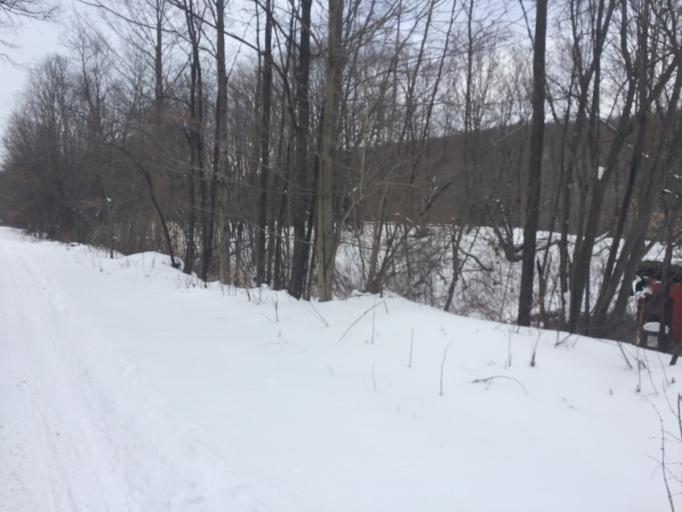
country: US
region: New York
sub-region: Cattaraugus County
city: Little Valley
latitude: 42.2524
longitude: -78.7987
